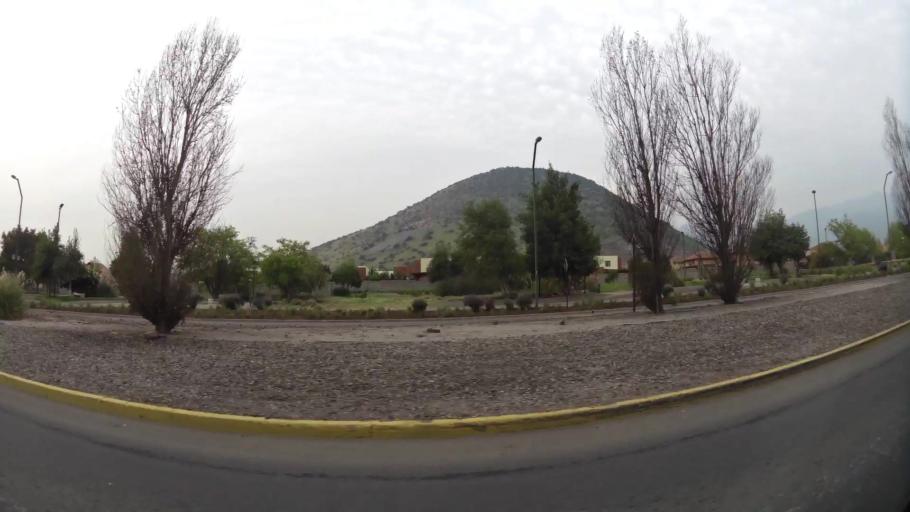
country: CL
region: Santiago Metropolitan
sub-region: Provincia de Chacabuco
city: Chicureo Abajo
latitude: -33.3117
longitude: -70.6574
